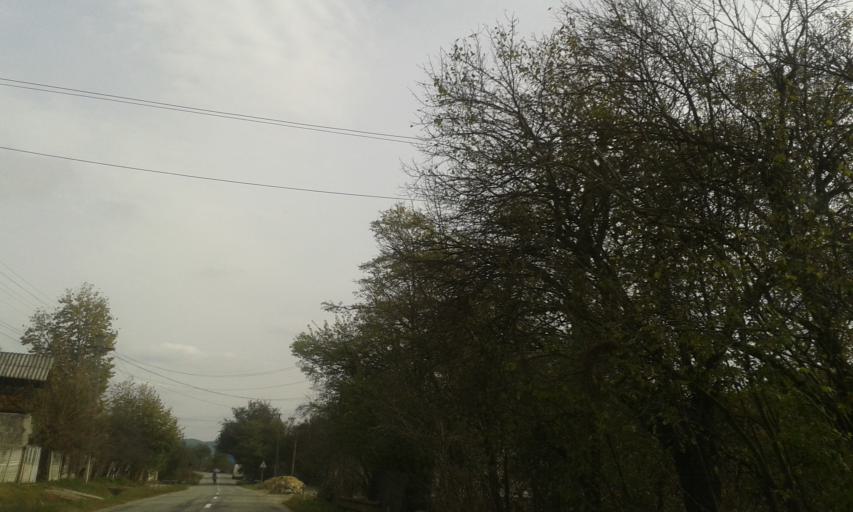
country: RO
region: Valcea
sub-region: Comuna Gradistea
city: Gradistea
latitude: 44.9014
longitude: 23.8064
